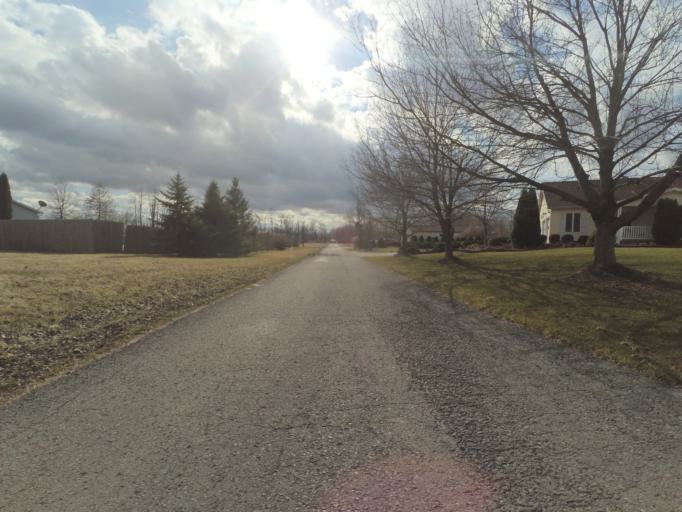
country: US
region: Pennsylvania
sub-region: Centre County
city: Stormstown
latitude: 40.8024
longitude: -77.9920
